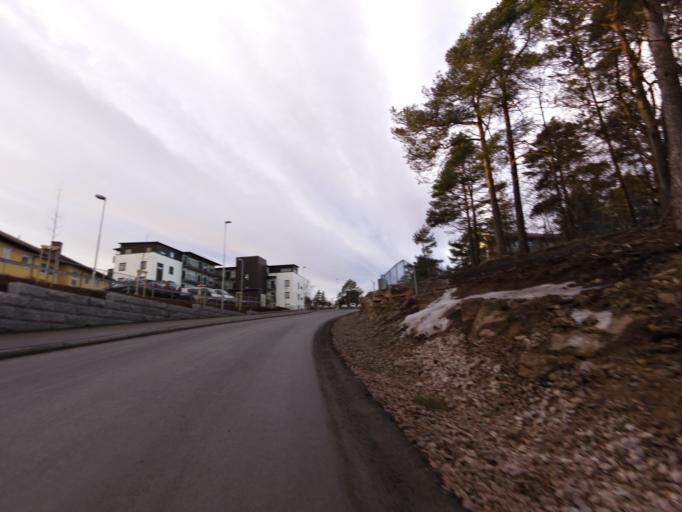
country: NO
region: Ostfold
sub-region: Fredrikstad
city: Fredrikstad
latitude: 59.2280
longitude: 10.9523
